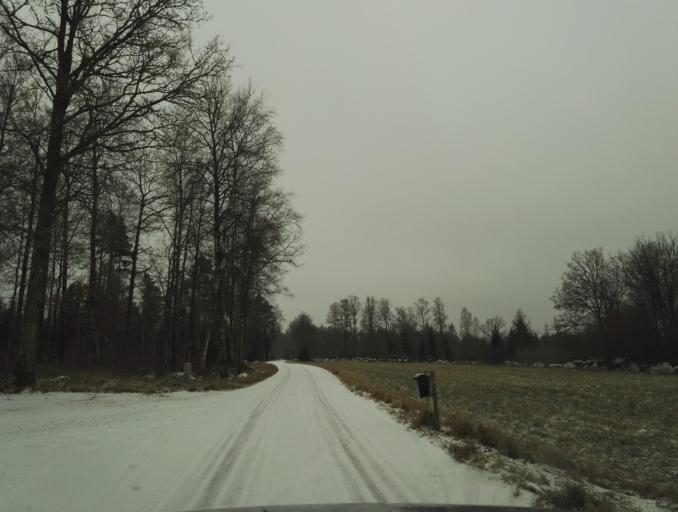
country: SE
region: Kronoberg
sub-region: Alvesta Kommun
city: Vislanda
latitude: 56.7024
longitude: 14.4172
